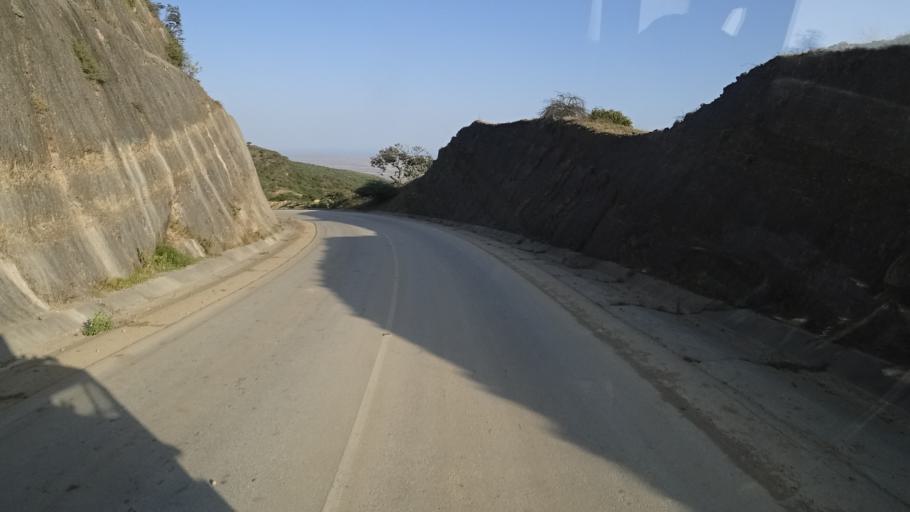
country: OM
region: Zufar
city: Salalah
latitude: 17.0613
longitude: 54.6061
